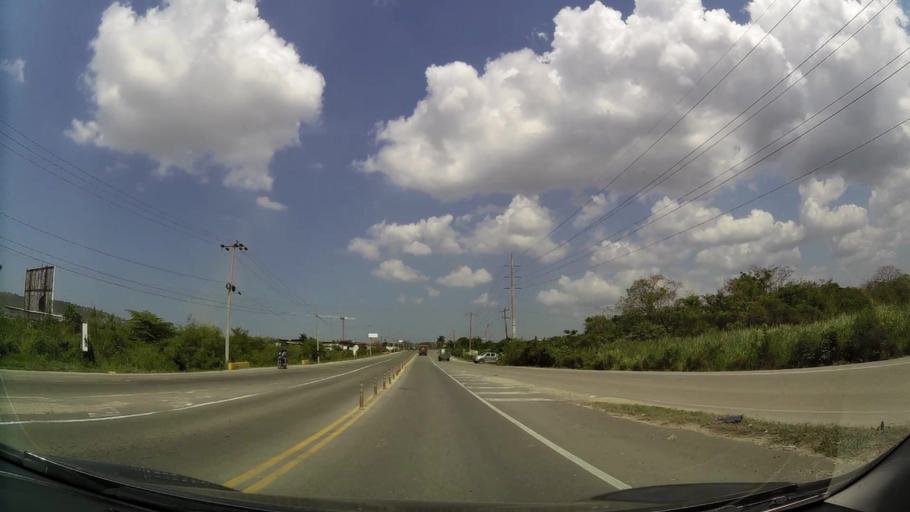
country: CO
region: Bolivar
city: Cartagena
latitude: 10.3450
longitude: -75.4840
